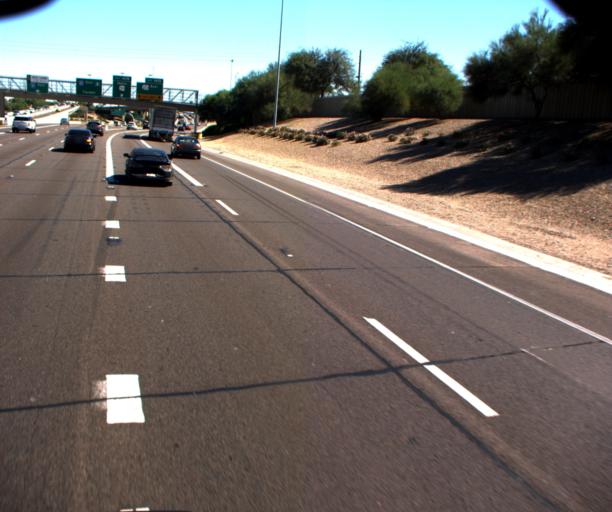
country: US
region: Arizona
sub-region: Maricopa County
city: Phoenix
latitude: 33.4618
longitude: -112.0450
